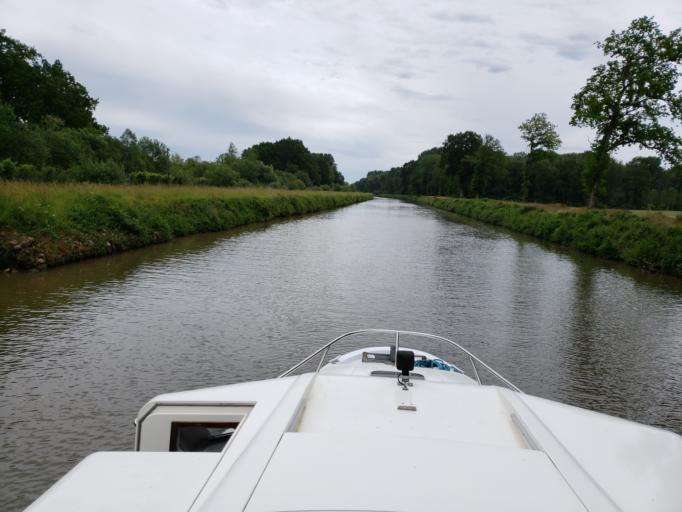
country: FR
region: Bourgogne
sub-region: Departement de l'Yonne
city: Appoigny
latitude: 47.9039
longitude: 3.5344
